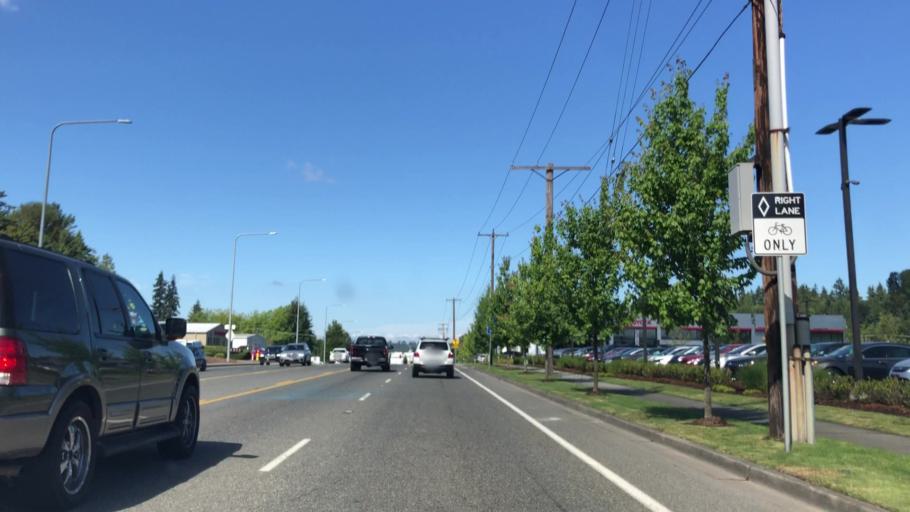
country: US
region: Washington
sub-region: King County
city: Kingsgate
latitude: 47.7115
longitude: -122.1629
